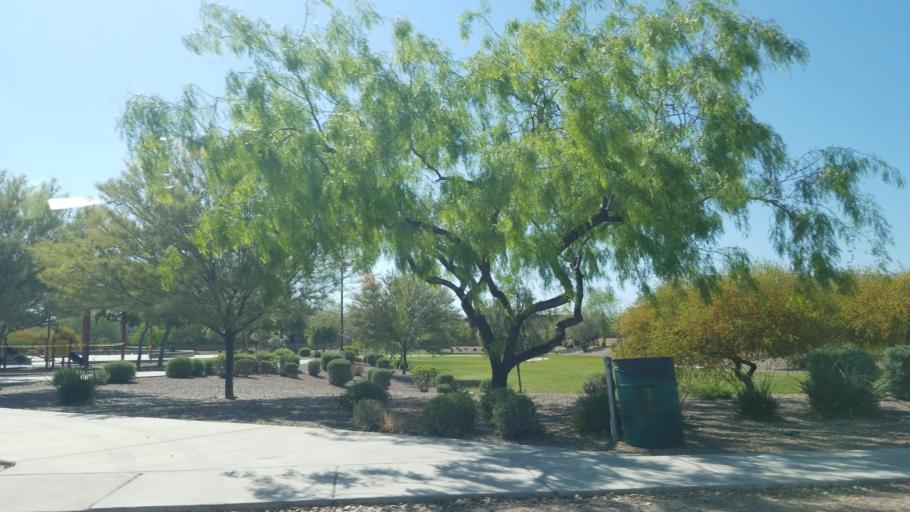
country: US
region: Arizona
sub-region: Maricopa County
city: Glendale
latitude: 33.5610
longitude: -112.1950
